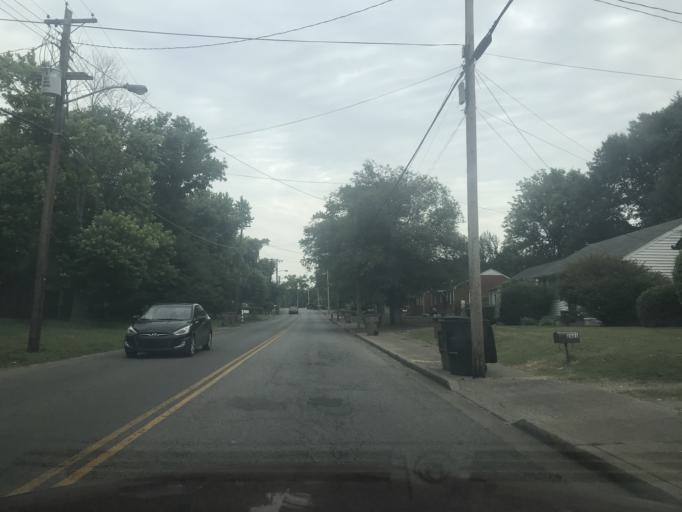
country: US
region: Tennessee
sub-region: Davidson County
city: Nashville
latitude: 36.1806
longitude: -86.8215
